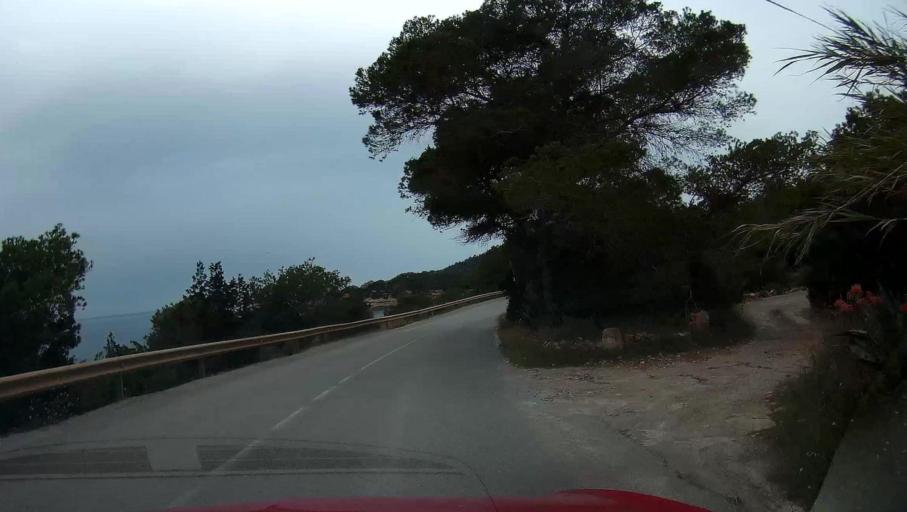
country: ES
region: Balearic Islands
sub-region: Illes Balears
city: Sant Josep de sa Talaia
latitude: 38.8696
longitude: 1.3390
